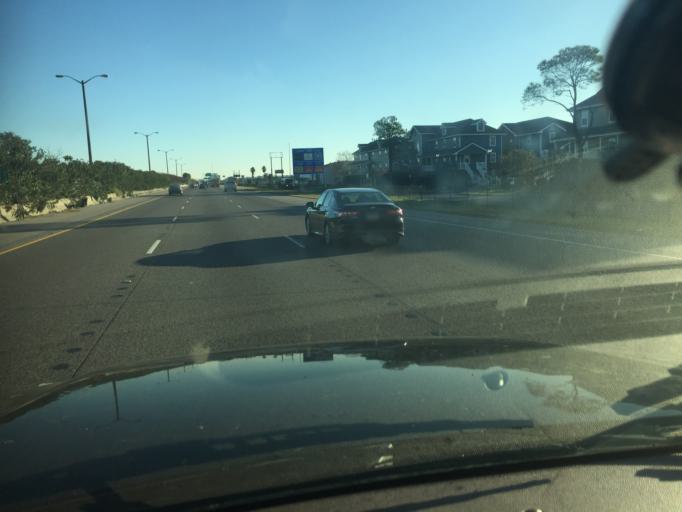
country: US
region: Louisiana
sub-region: Saint Bernard Parish
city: Arabi
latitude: 30.0321
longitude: -89.9881
